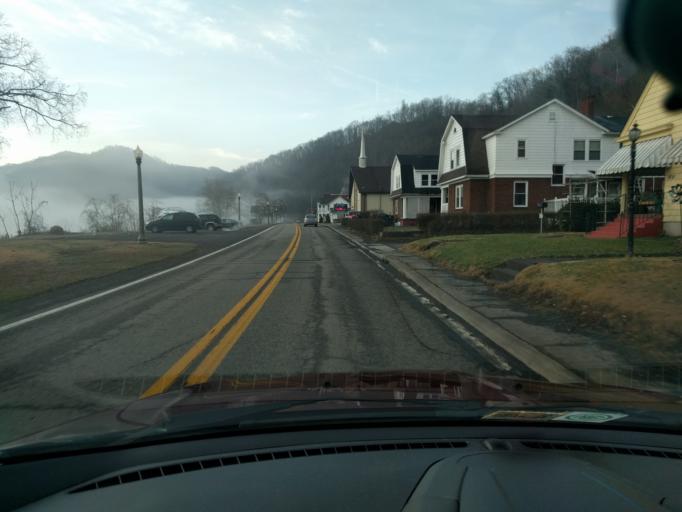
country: US
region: West Virginia
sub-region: Kanawha County
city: Montgomery
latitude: 38.1535
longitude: -81.2150
